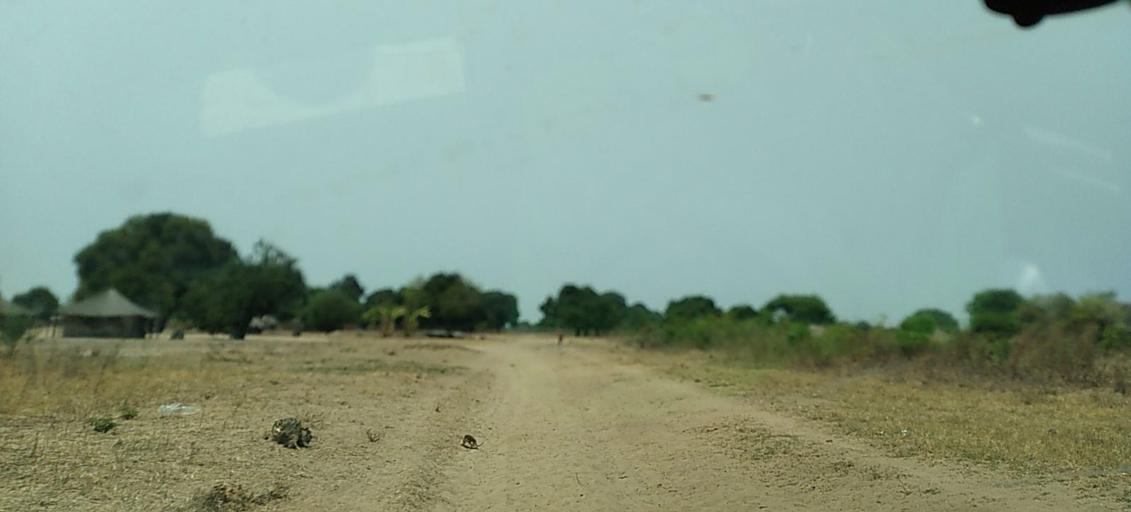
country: ZM
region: Western
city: Lukulu
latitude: -14.1552
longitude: 23.3047
